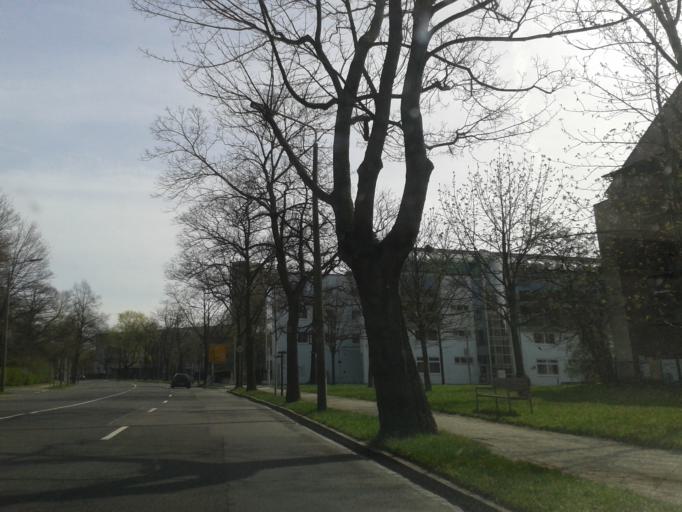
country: DE
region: Saxony
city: Dresden
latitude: 51.0407
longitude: 13.7430
